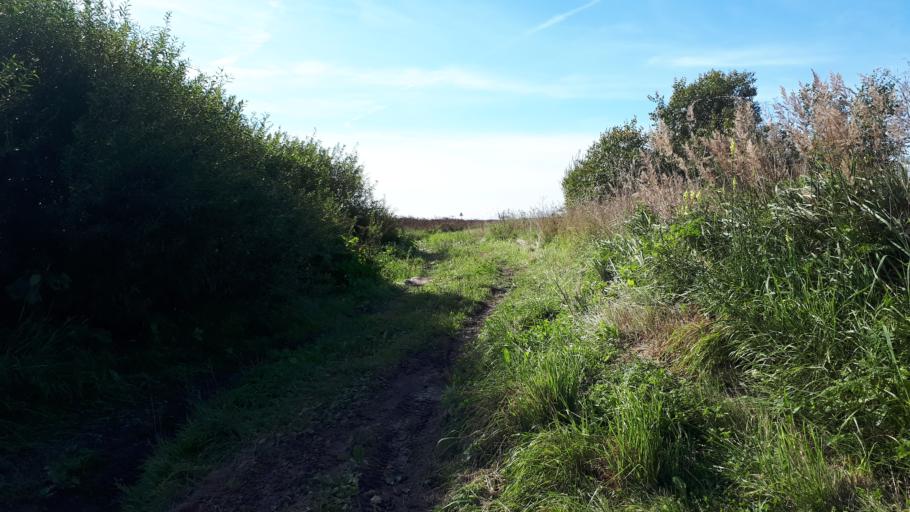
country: RU
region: Jaroslavl
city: Tunoshna
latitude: 57.6591
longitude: 40.0508
